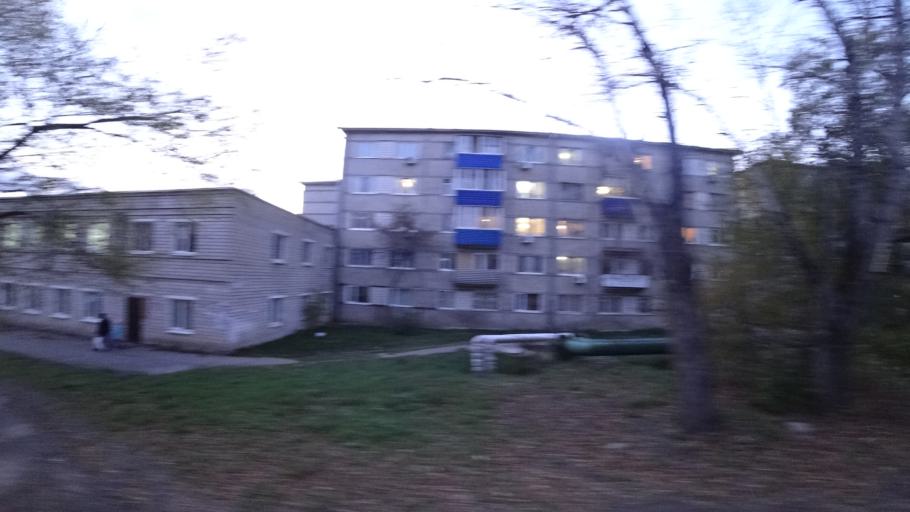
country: RU
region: Khabarovsk Krai
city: Amursk
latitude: 50.2158
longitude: 136.9012
